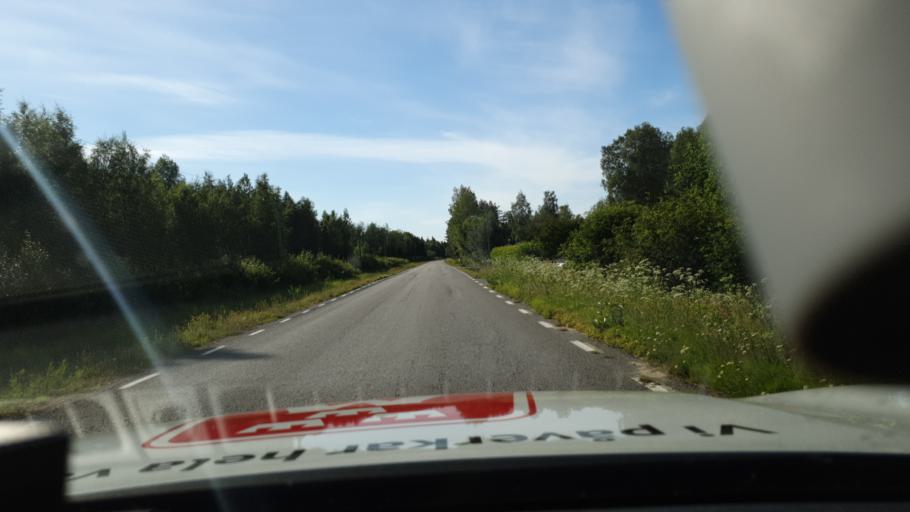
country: SE
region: Norrbotten
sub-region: Kalix Kommun
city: Toere
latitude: 65.8911
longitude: 22.6433
